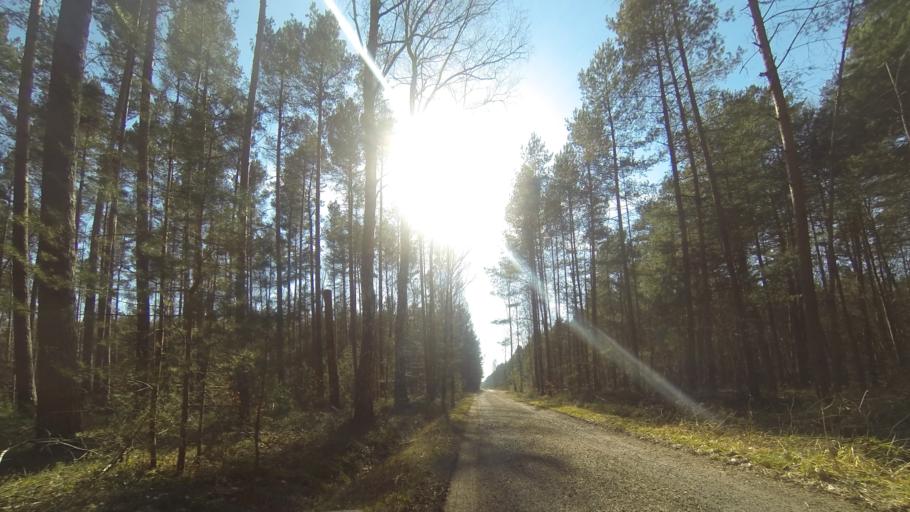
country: DE
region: Saxony
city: Tauscha
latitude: 51.2471
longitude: 13.8317
